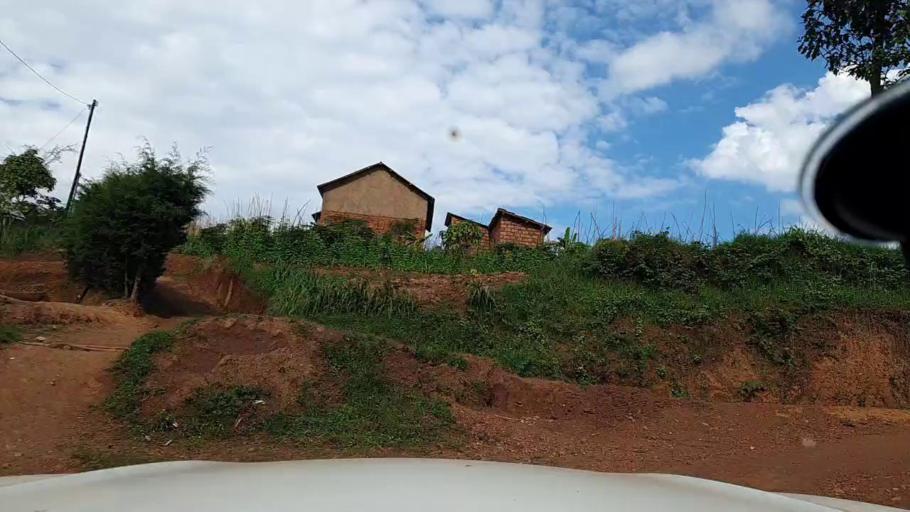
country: RW
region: Kigali
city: Kigali
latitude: -1.7913
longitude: 29.8266
